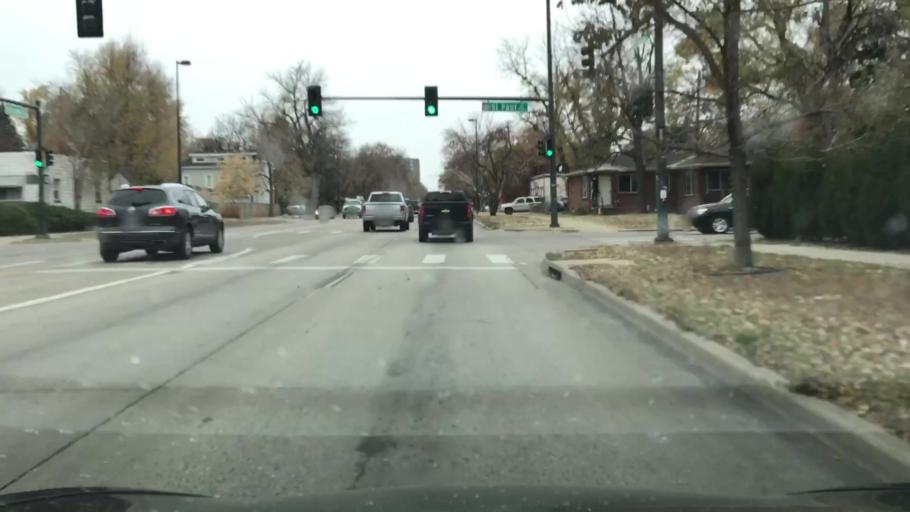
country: US
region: Colorado
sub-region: Arapahoe County
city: Glendale
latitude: 39.6785
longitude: -104.9505
